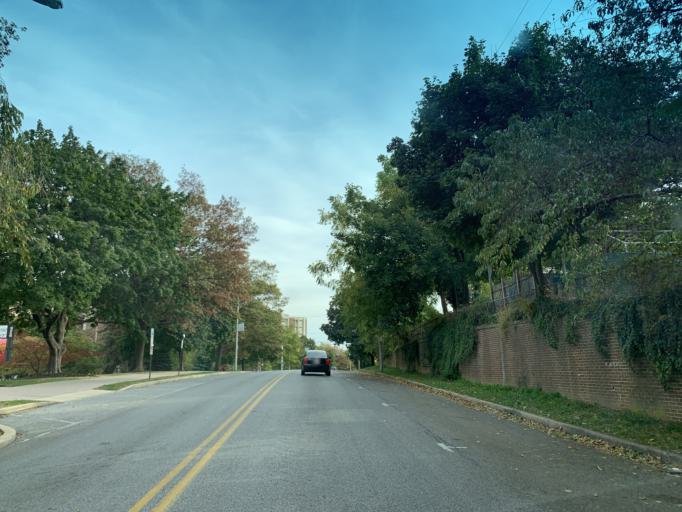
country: US
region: Pennsylvania
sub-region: York County
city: York
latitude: 39.9646
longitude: -76.7188
